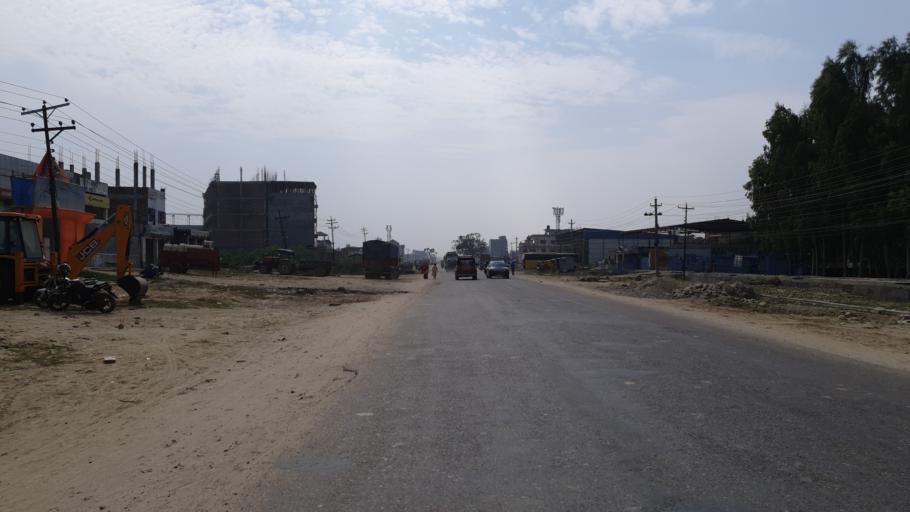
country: NP
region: Central Region
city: Janakpur
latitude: 26.7515
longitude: 85.9250
